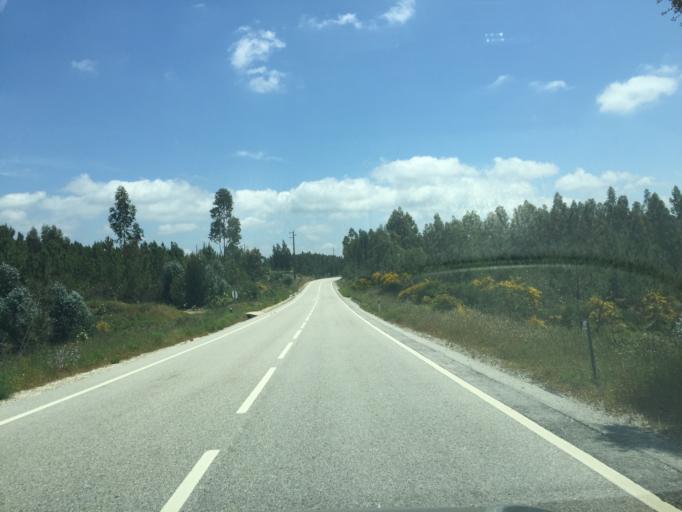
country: PT
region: Castelo Branco
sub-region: Vila de Rei
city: Vila de Rei
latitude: 39.7071
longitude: -8.1324
